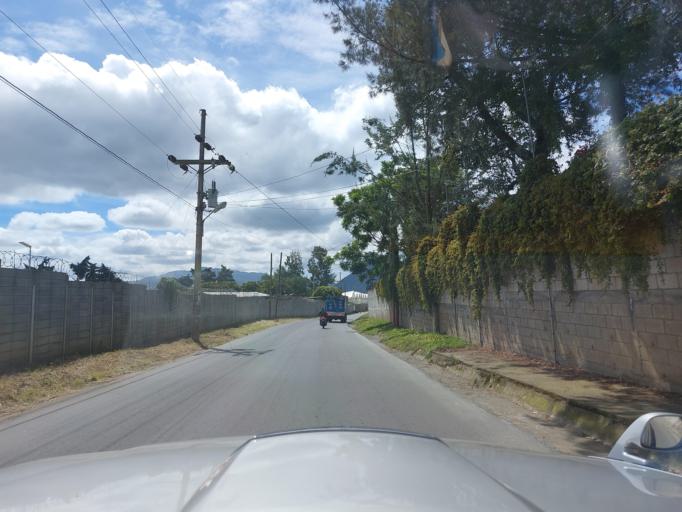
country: GT
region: Chimaltenango
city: San Andres Itzapa
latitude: 14.6166
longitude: -90.8253
